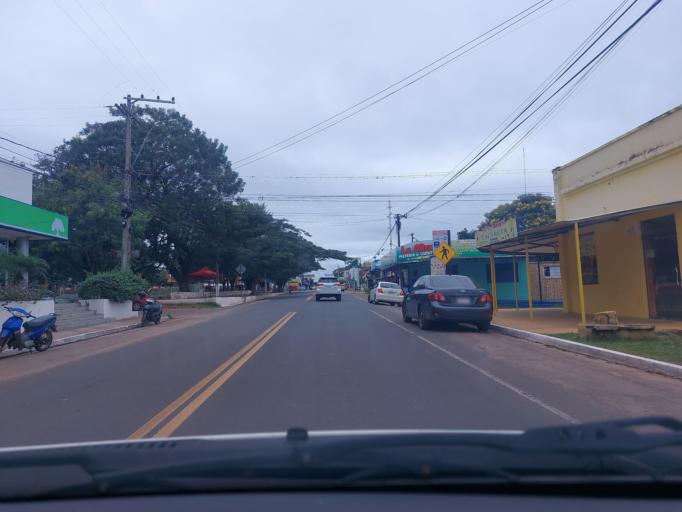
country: PY
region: San Pedro
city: Guayaybi
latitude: -24.6703
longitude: -56.4456
